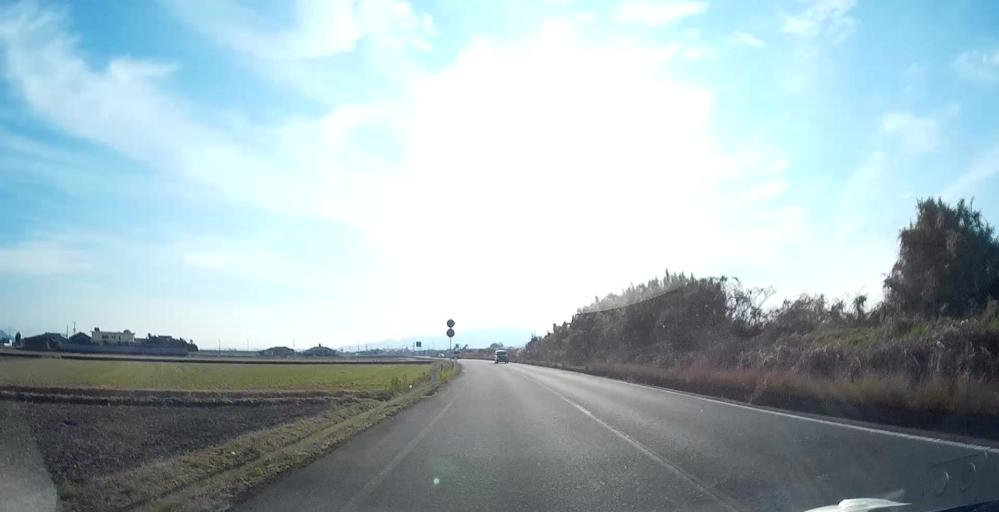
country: JP
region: Kumamoto
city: Uto
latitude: 32.7367
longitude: 130.6648
